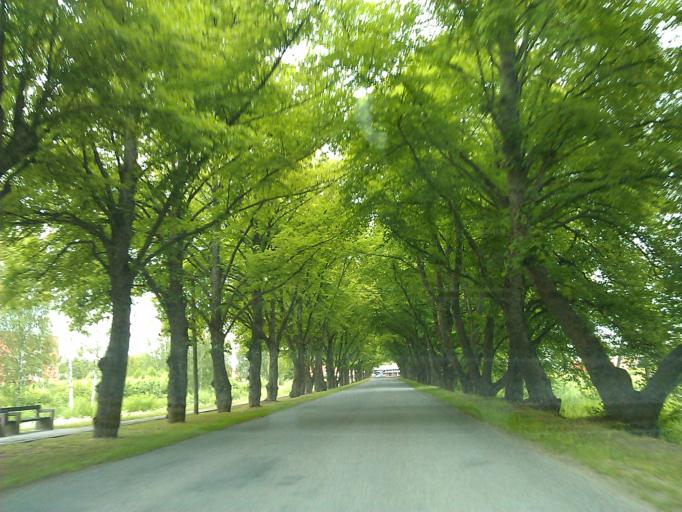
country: LV
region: Kuldigas Rajons
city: Kuldiga
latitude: 56.9648
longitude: 21.9542
